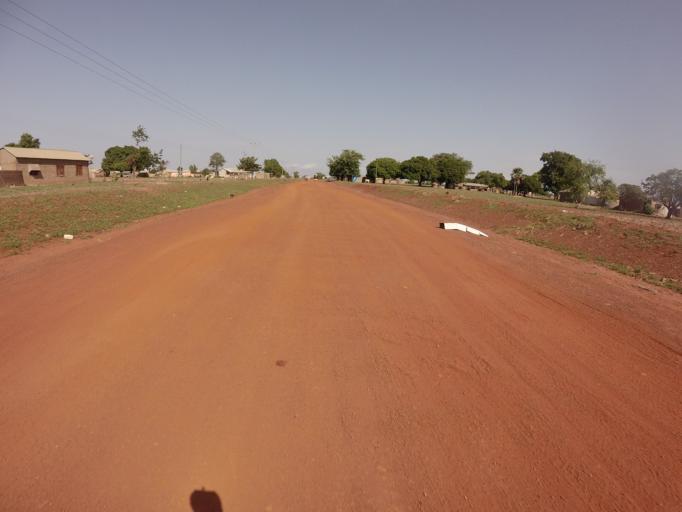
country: GH
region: Upper East
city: Bawku
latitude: 10.8346
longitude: -0.1744
